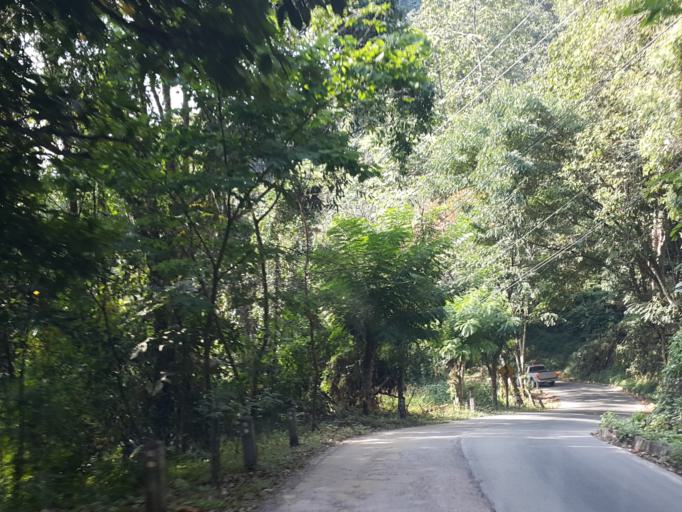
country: TH
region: Chiang Mai
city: Mae On
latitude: 18.8666
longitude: 99.3353
